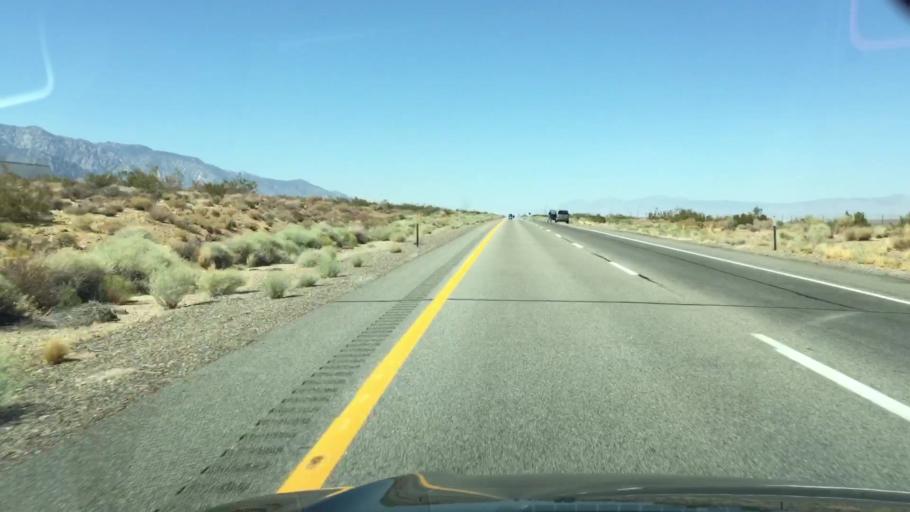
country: US
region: California
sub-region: Inyo County
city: Lone Pine
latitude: 36.1333
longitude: -117.9731
